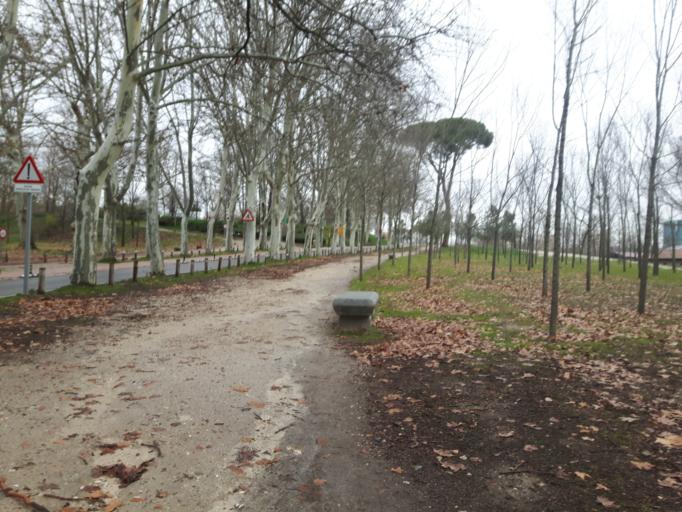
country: ES
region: Madrid
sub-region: Provincia de Madrid
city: Moncloa-Aravaca
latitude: 40.4191
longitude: -3.7288
